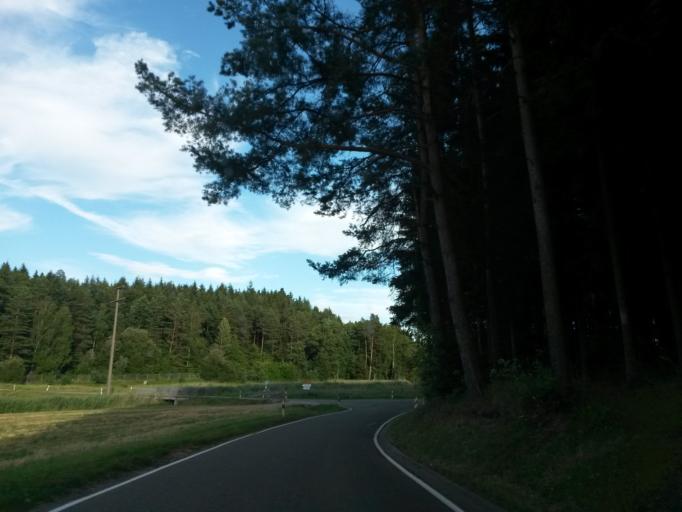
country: DE
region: Baden-Wuerttemberg
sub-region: Regierungsbezirk Stuttgart
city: Ellenberg
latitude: 49.0439
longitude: 10.2389
